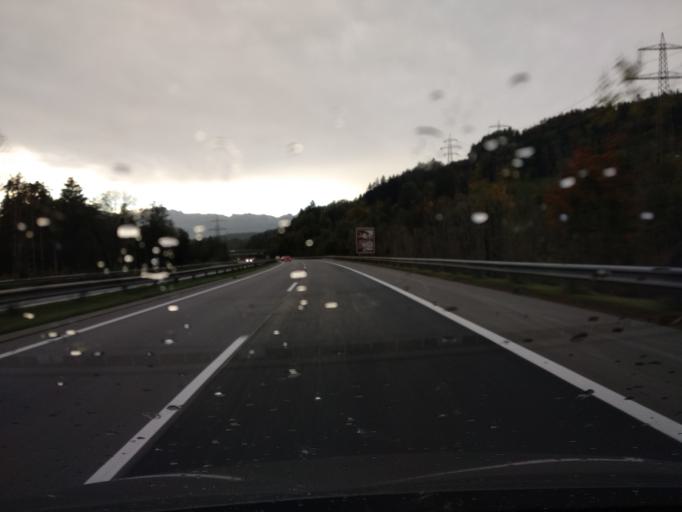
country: AT
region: Vorarlberg
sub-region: Politischer Bezirk Feldkirch
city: Gofis
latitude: 47.2237
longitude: 9.6487
